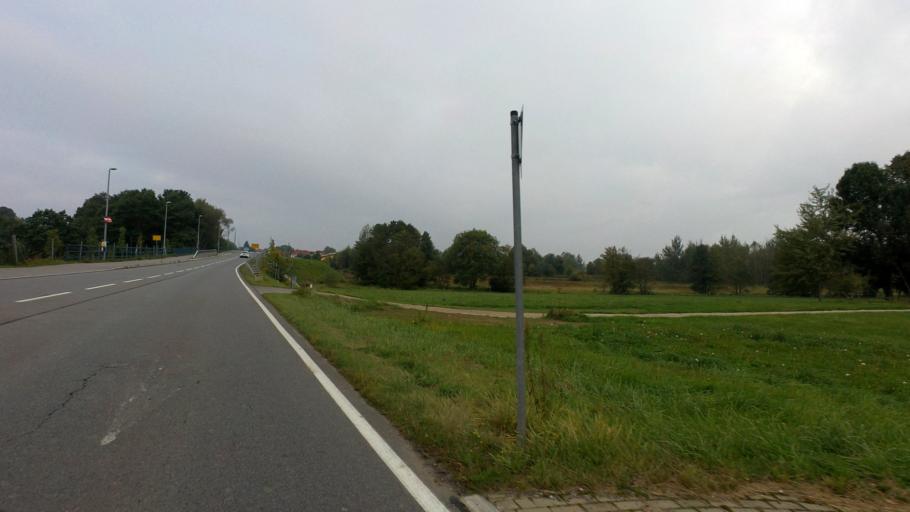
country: DE
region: Saxony
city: Arnsdorf
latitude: 51.0896
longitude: 14.0100
